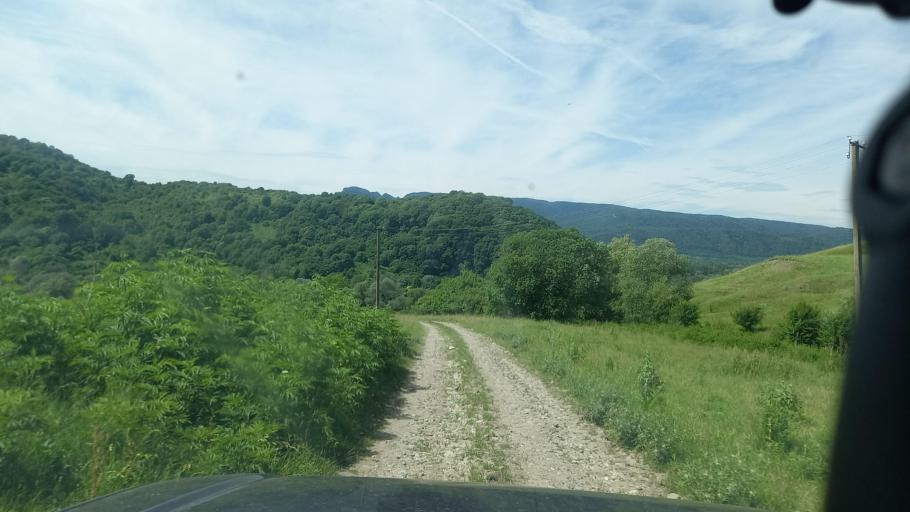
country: RU
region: Karachayevo-Cherkesiya
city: Kurdzhinovo
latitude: 44.1449
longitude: 41.0584
